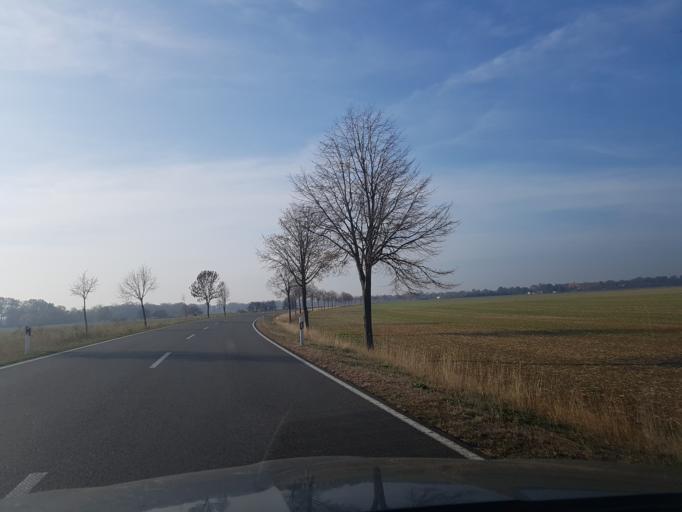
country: DE
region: Saxony
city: Beilrode
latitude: 51.5473
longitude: 13.0802
